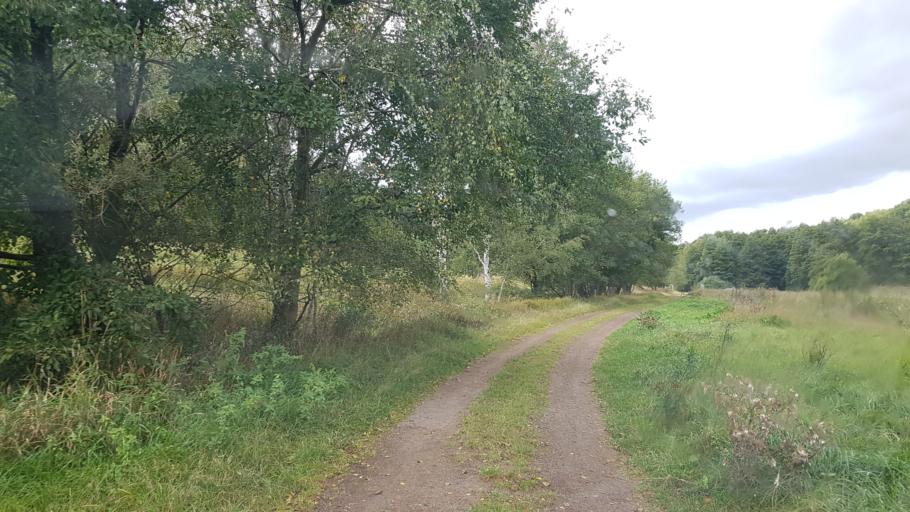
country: DE
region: Saxony
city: Dahlen
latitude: 51.3658
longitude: 13.0142
